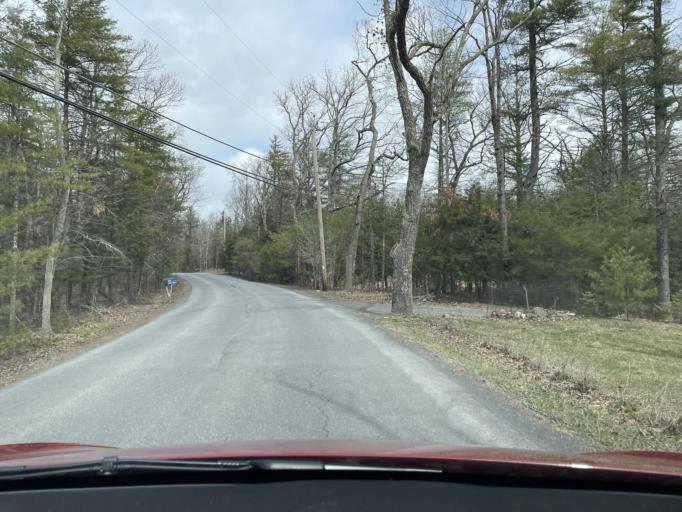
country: US
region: New York
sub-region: Ulster County
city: Zena
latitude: 42.0343
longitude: -74.0373
